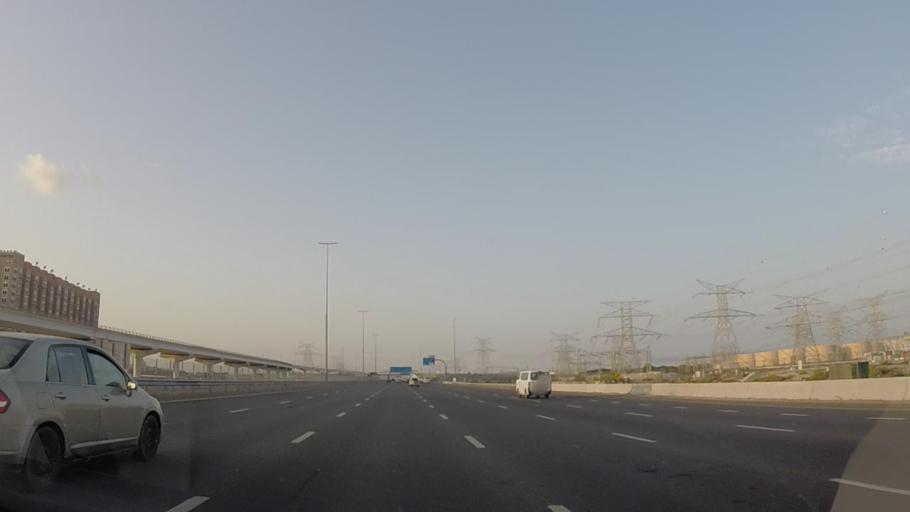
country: AE
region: Dubai
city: Dubai
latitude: 25.0452
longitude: 55.1154
